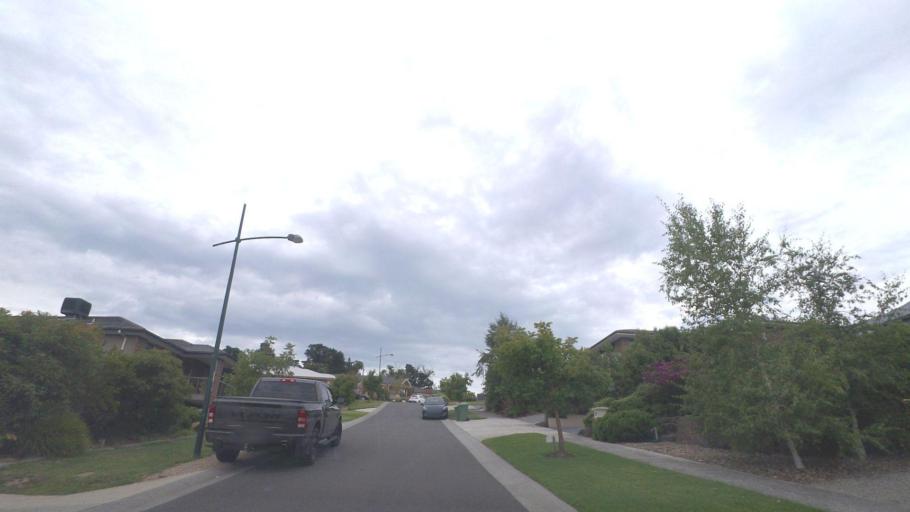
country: AU
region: Victoria
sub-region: Yarra Ranges
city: Mount Evelyn
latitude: -37.7651
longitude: 145.3715
